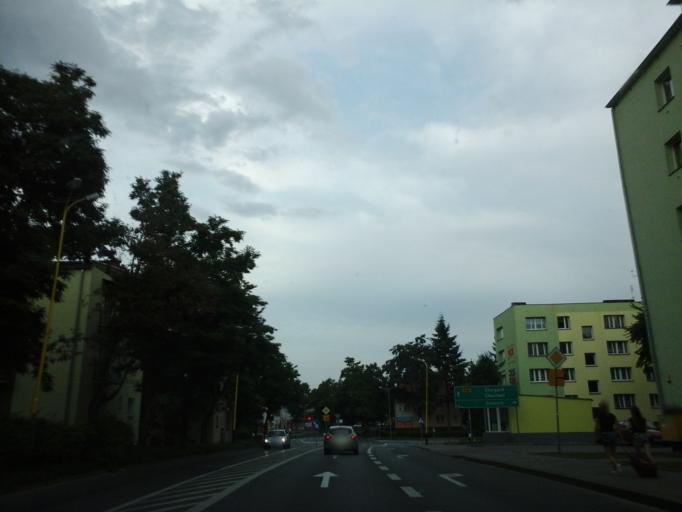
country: PL
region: West Pomeranian Voivodeship
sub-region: Powiat goleniowski
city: Nowogard
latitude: 53.6704
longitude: 15.1211
